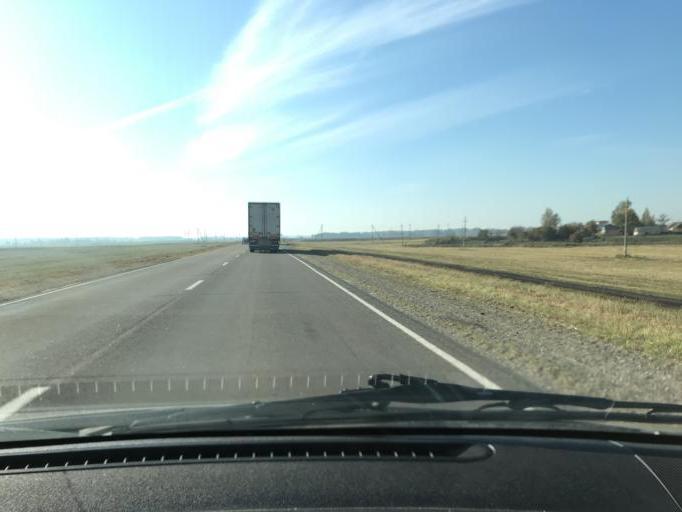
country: BY
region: Brest
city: Asnyezhytsy
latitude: 52.2834
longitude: 26.4067
